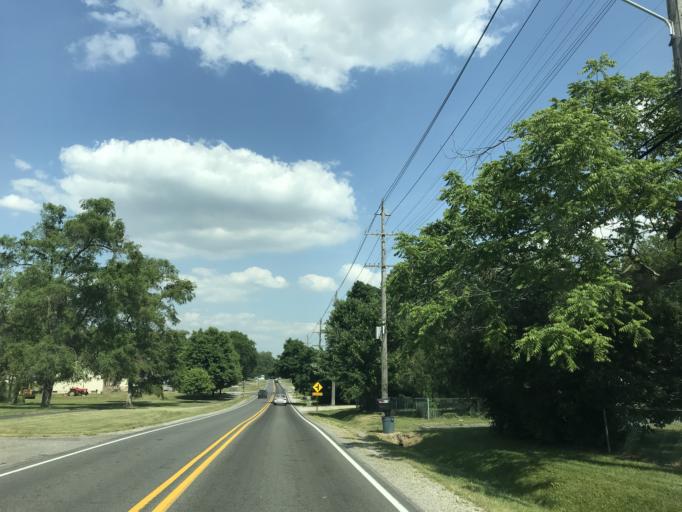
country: US
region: Michigan
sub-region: Washtenaw County
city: Ypsilanti
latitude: 42.2611
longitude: -83.5961
